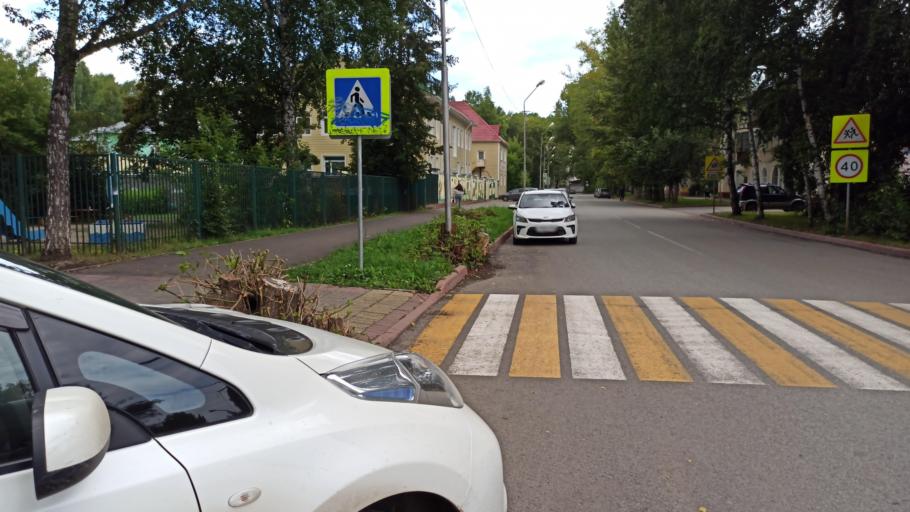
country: RU
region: Tomsk
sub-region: Tomskiy Rayon
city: Tomsk
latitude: 56.4620
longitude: 84.9842
